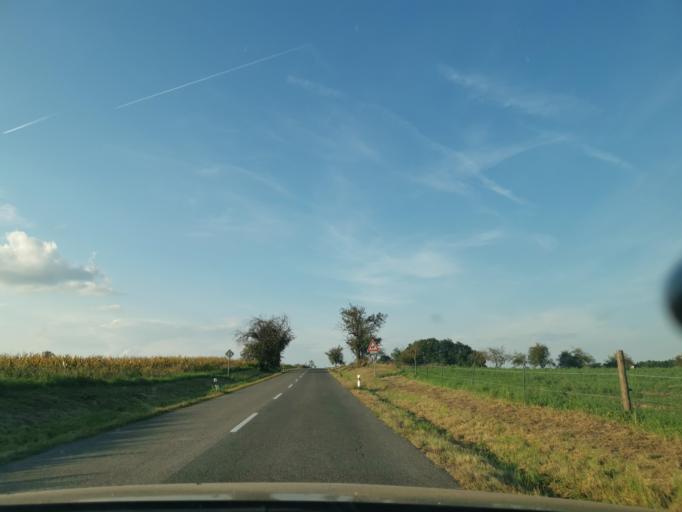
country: SK
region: Trnavsky
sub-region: Okres Senica
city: Senica
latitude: 48.6841
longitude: 17.2716
